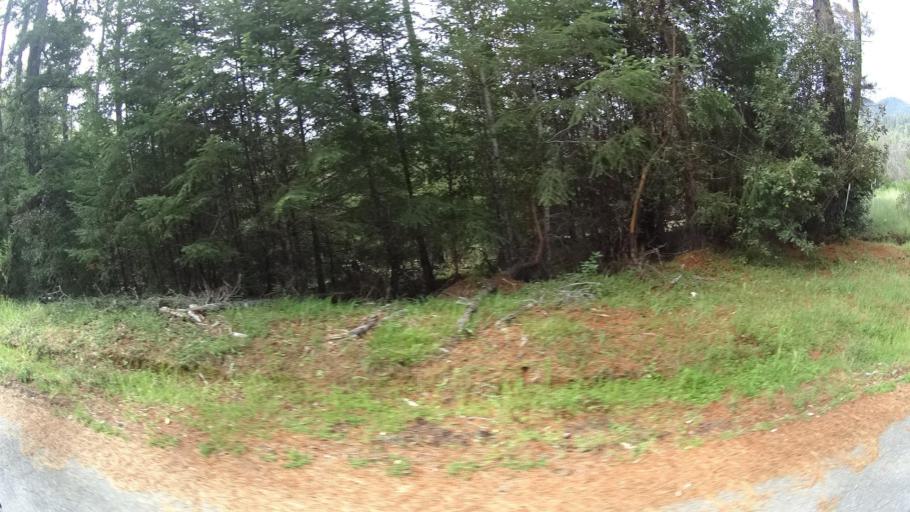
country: US
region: California
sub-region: Humboldt County
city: Redway
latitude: 40.0629
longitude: -123.8321
